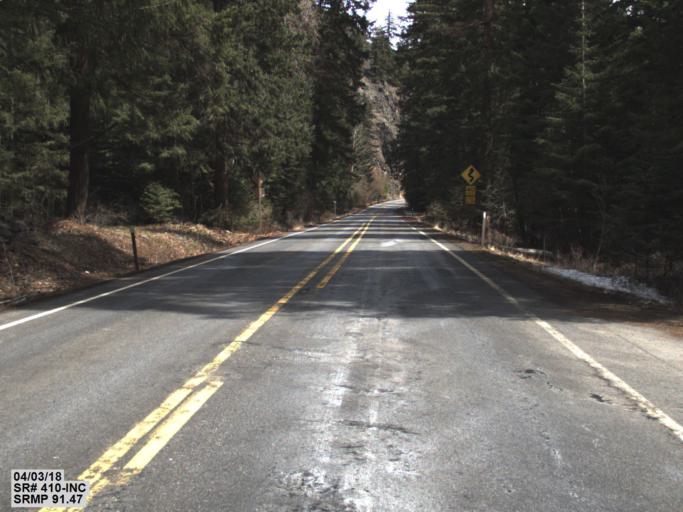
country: US
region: Washington
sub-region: Kittitas County
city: Cle Elum
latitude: 46.9867
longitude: -121.1090
